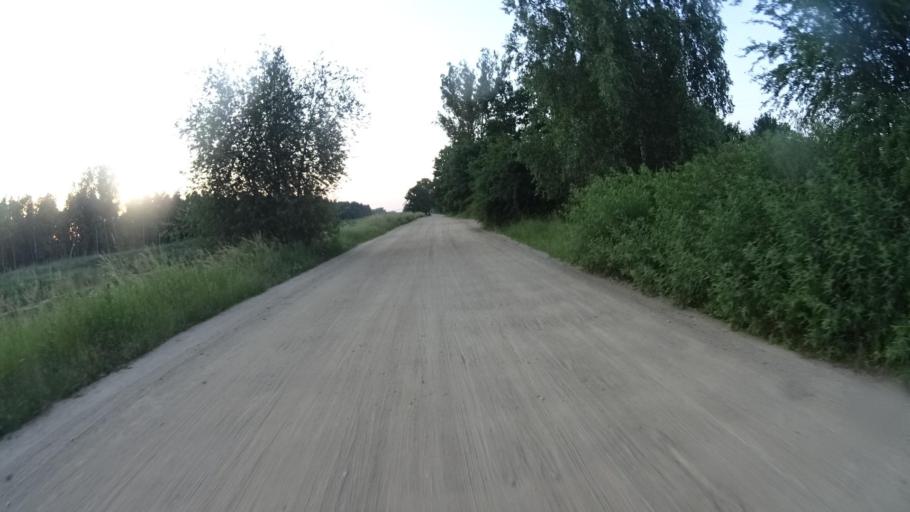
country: PL
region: Masovian Voivodeship
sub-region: Powiat legionowski
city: Stanislawow Pierwszy
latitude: 52.3471
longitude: 21.0341
